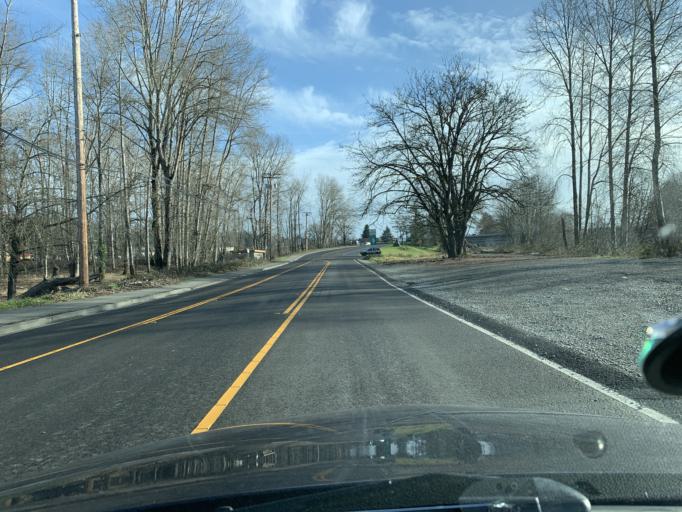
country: US
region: Washington
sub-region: Pierce County
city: North Puyallup
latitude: 47.2038
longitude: -122.2970
